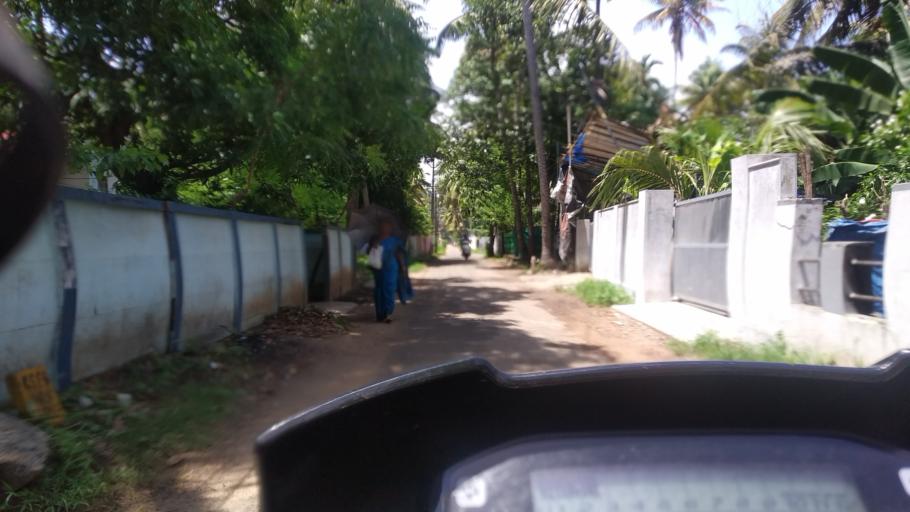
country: IN
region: Kerala
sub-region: Ernakulam
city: Elur
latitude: 10.0724
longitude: 76.2090
